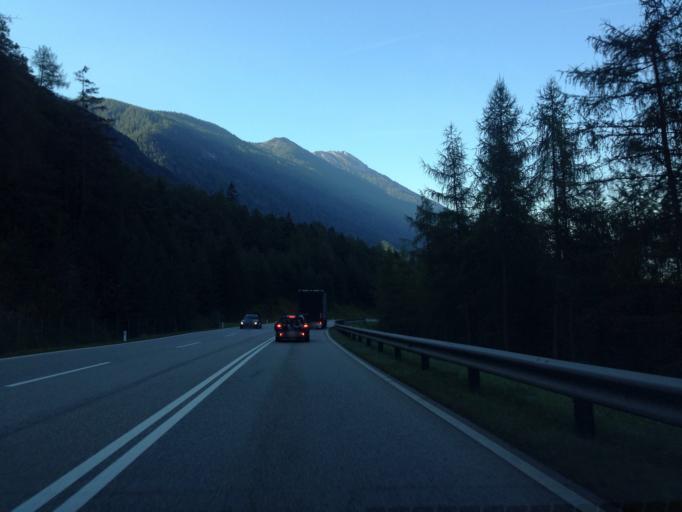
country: AT
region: Tyrol
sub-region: Politischer Bezirk Imst
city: Nassereith
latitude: 47.2968
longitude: 10.8506
